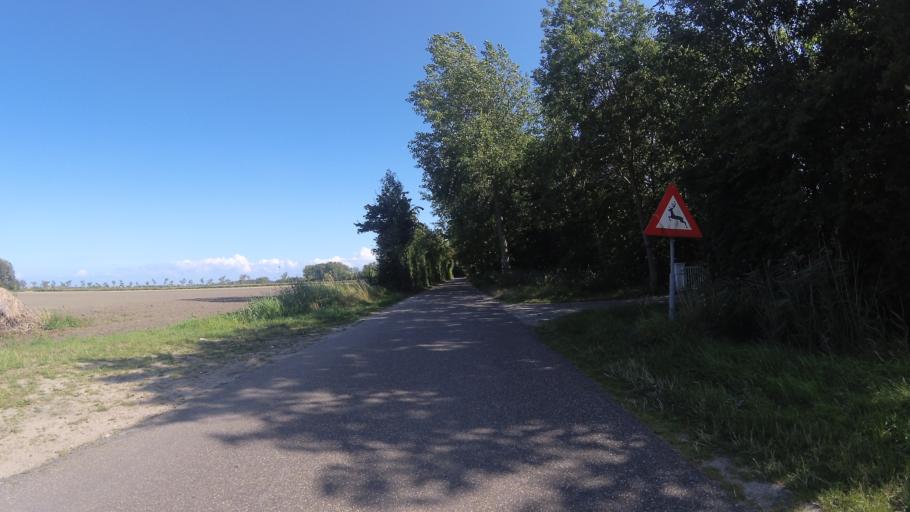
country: NL
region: Zeeland
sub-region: Gemeente Middelburg
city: Middelburg
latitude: 51.5637
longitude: 3.5086
